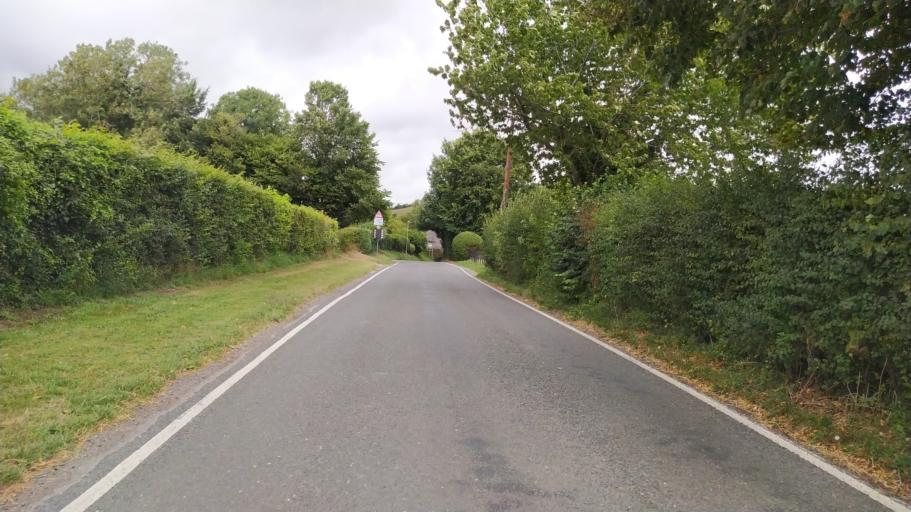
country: GB
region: England
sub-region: Hampshire
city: Petersfield
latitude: 50.9912
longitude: -1.0278
